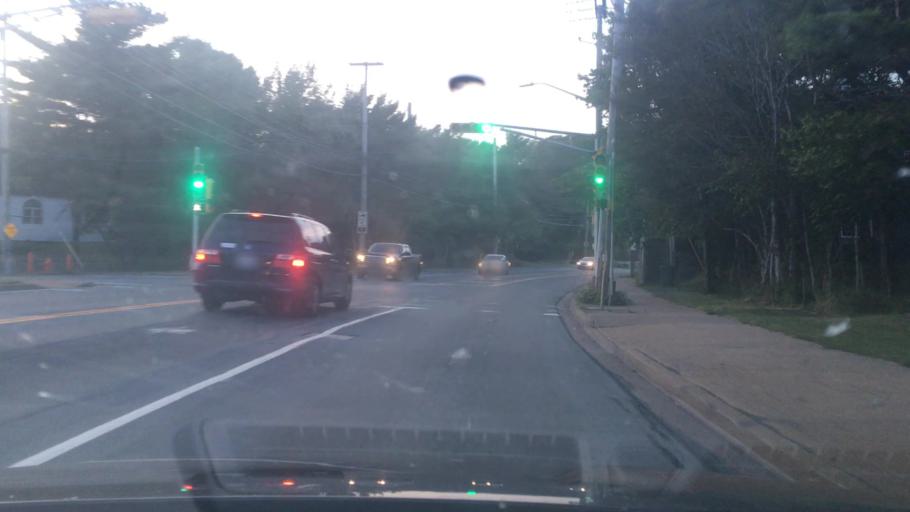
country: CA
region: Nova Scotia
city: Dartmouth
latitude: 44.6821
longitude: -63.6602
